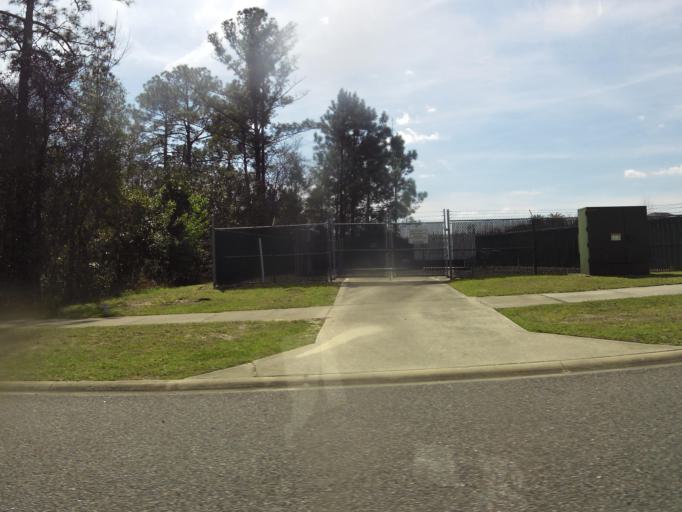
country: US
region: Florida
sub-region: Clay County
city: Middleburg
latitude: 30.0979
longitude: -81.8553
